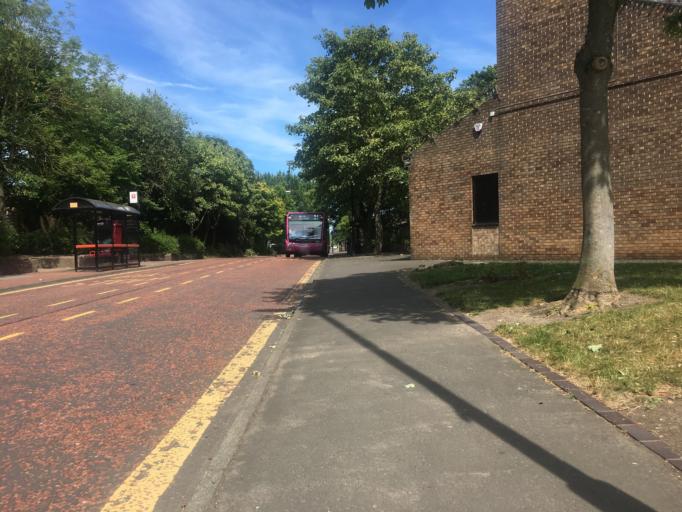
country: GB
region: England
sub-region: County Durham
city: Chester-le-Street
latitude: 54.8789
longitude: -1.5506
